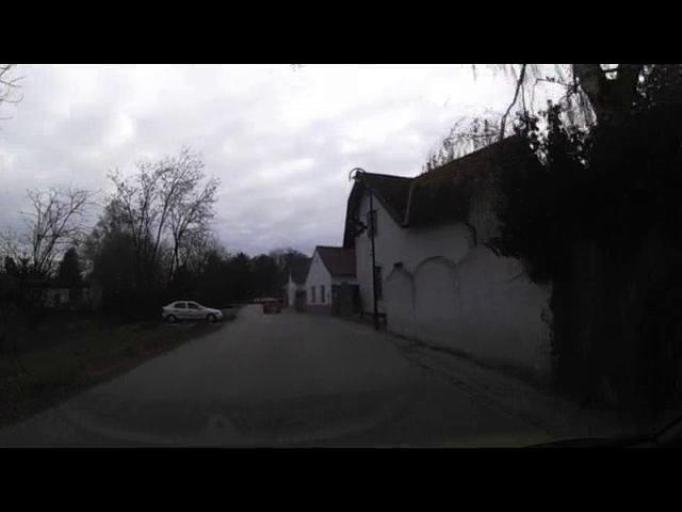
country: AT
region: Lower Austria
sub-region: Politischer Bezirk Wiener Neustadt
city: Ebenfurth
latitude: 47.8999
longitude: 16.3510
